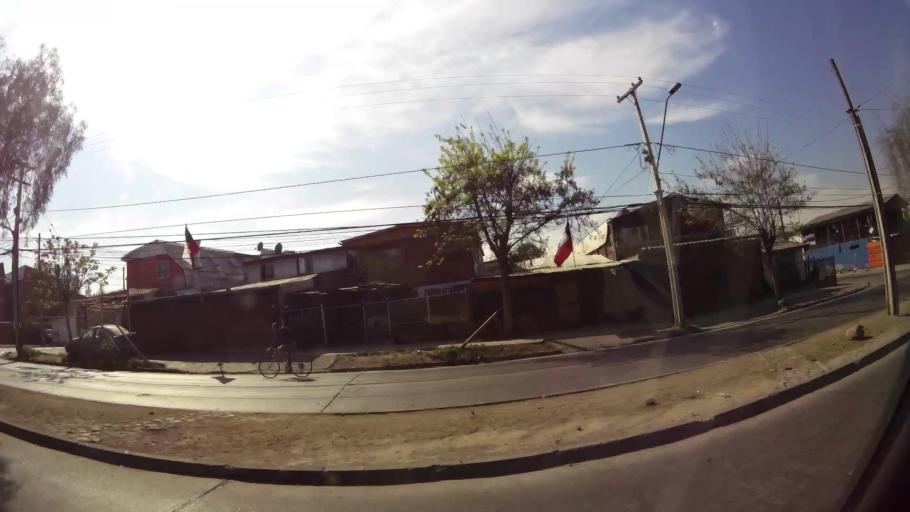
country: CL
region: Santiago Metropolitan
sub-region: Provincia de Santiago
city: Lo Prado
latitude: -33.4504
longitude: -70.7392
